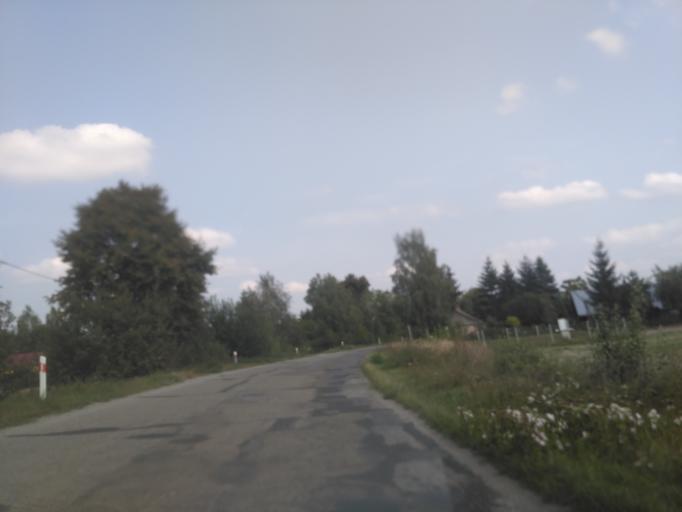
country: PL
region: Lublin Voivodeship
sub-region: Powiat wlodawski
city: Urszulin
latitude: 51.3792
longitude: 23.1703
